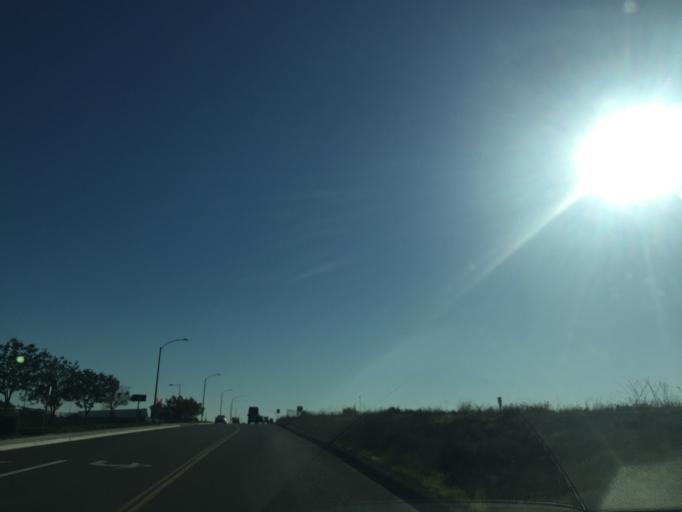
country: MX
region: Baja California
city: Tijuana
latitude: 32.5668
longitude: -116.9276
